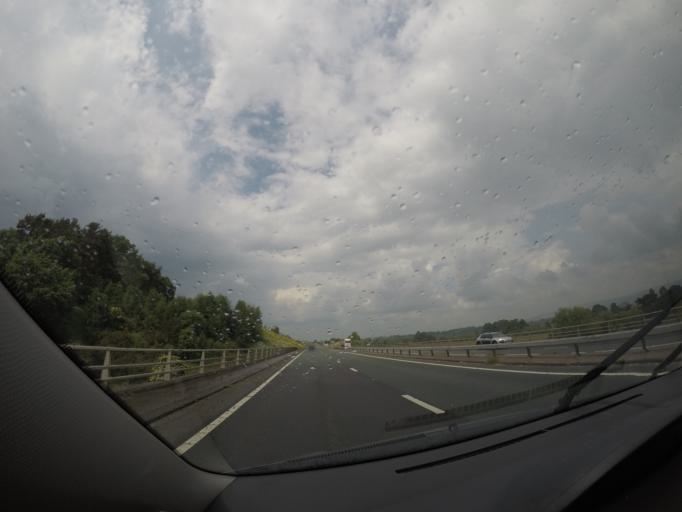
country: GB
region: England
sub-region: Cumbria
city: Appleby-in-Westmorland
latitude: 54.6401
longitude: -2.6150
